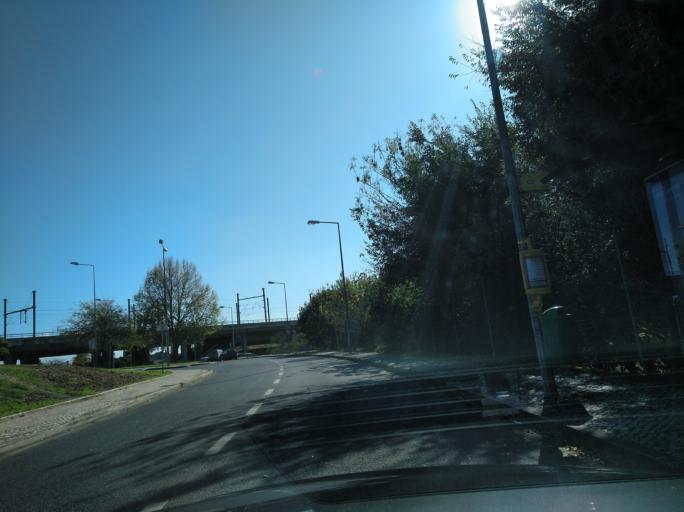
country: PT
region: Lisbon
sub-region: Loures
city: Moscavide
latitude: 38.7459
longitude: -9.1047
